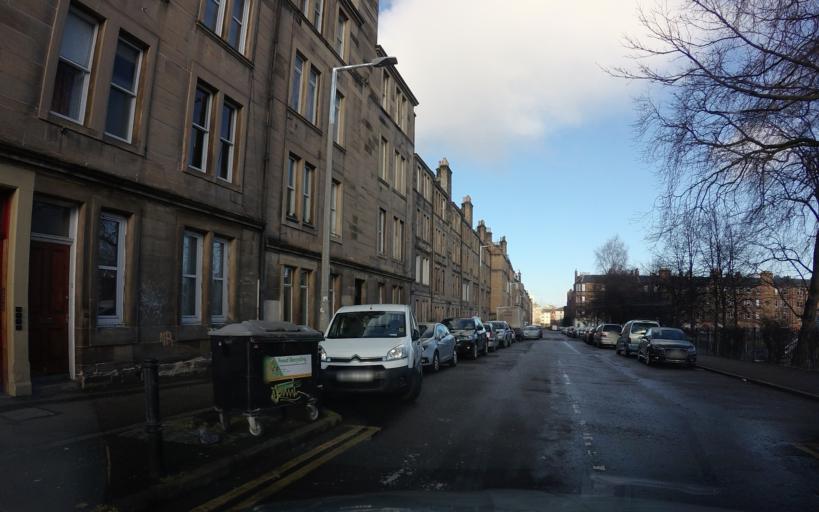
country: GB
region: Scotland
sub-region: West Lothian
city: Seafield
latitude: 55.9637
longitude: -3.1738
